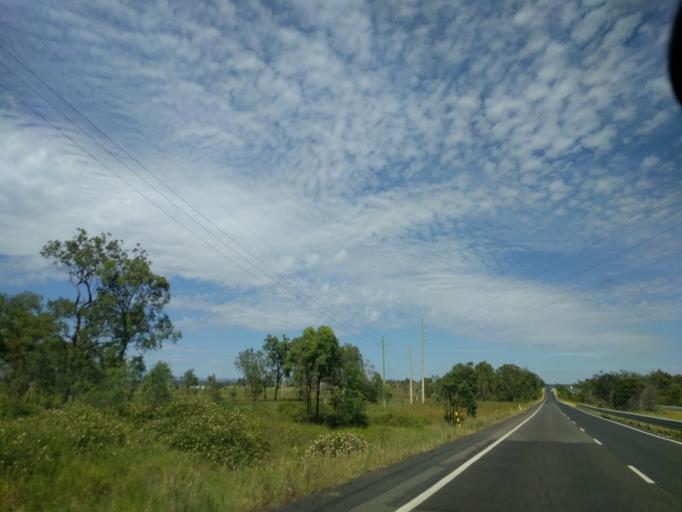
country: AU
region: Queensland
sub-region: Lockyer Valley
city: Gatton
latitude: -27.5373
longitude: 152.2721
